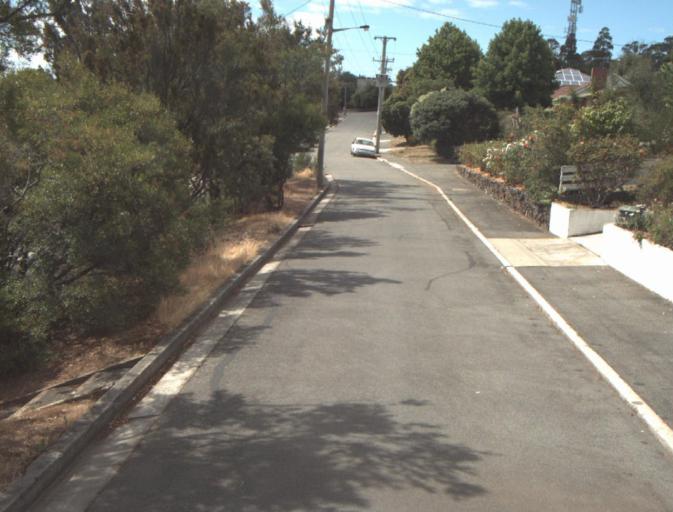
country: AU
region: Tasmania
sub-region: Launceston
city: West Launceston
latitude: -41.4522
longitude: 147.1242
